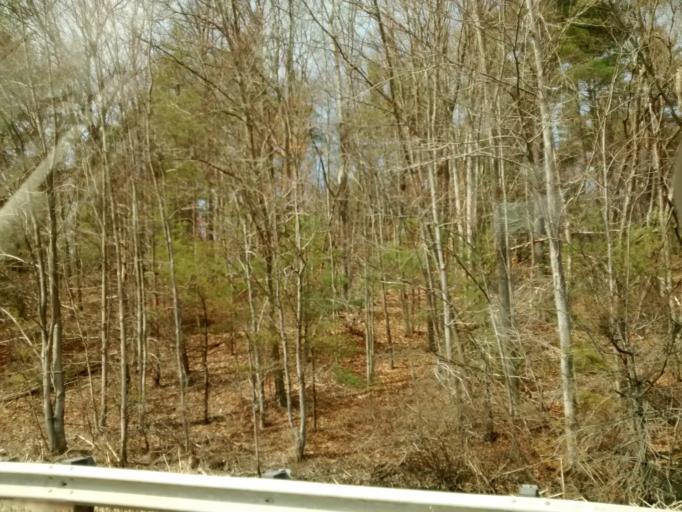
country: US
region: Massachusetts
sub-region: Worcester County
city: Charlton
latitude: 42.1462
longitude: -72.0145
